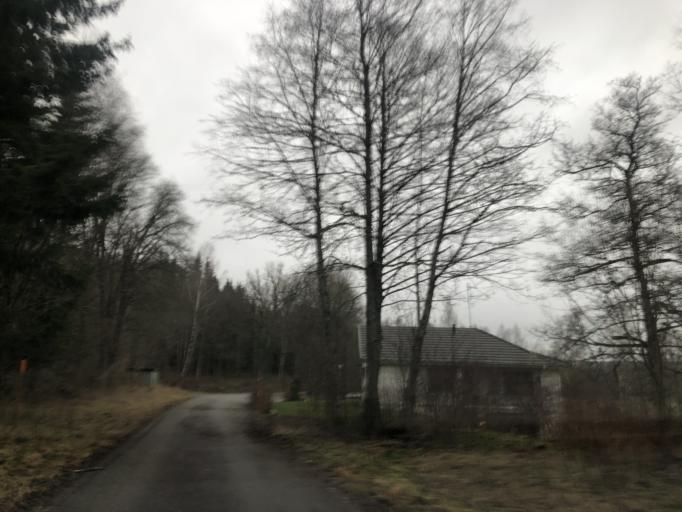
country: SE
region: Vaestra Goetaland
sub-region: Ulricehamns Kommun
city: Ulricehamn
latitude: 57.7909
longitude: 13.3916
